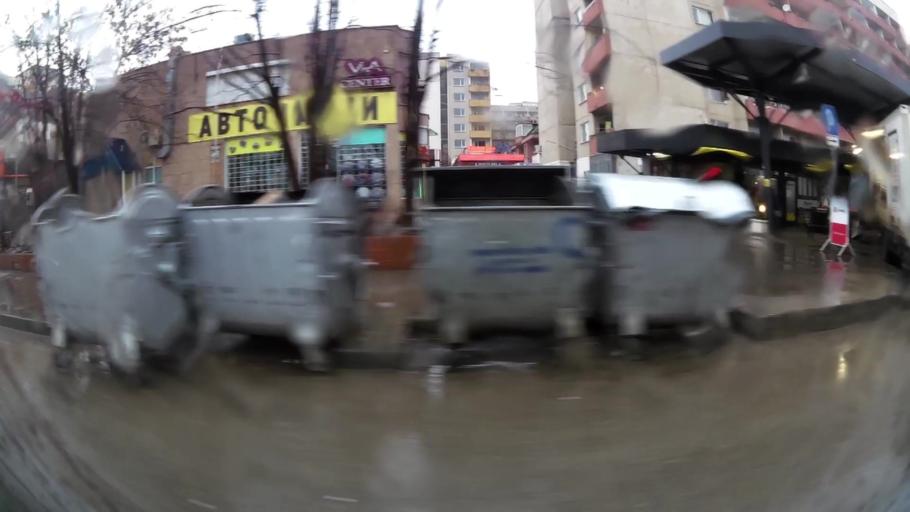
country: BG
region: Sofia-Capital
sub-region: Stolichna Obshtina
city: Sofia
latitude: 42.6433
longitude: 23.3418
